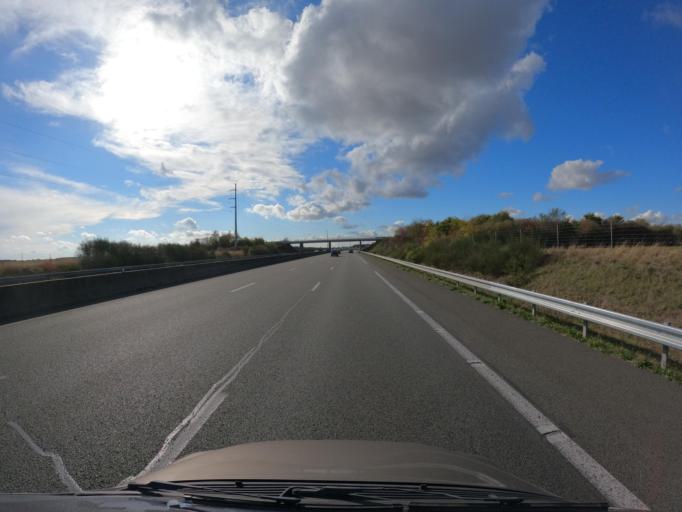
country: FR
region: Centre
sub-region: Departement d'Eure-et-Loir
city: Bailleau-le-Pin
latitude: 48.3307
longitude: 1.3833
